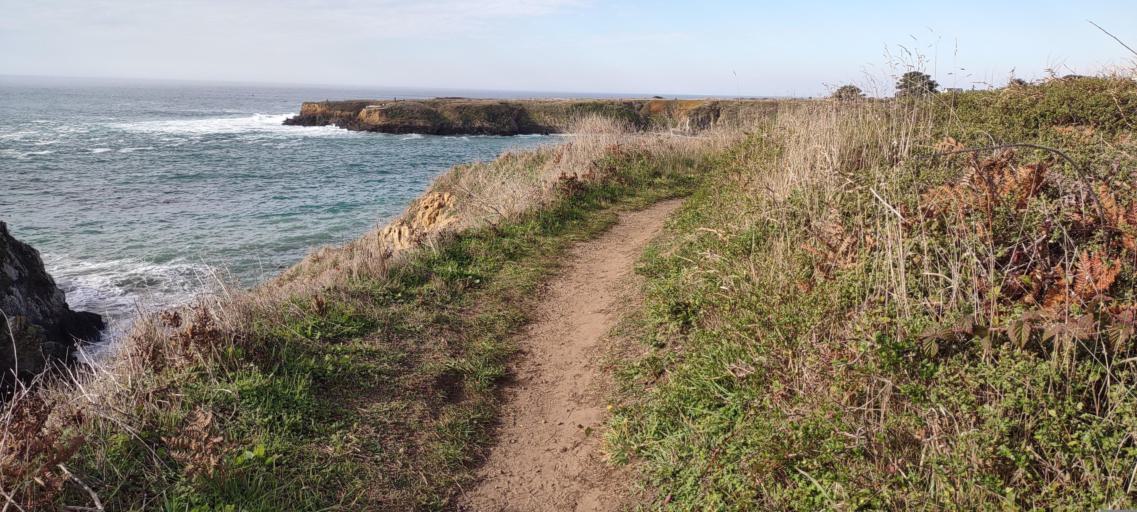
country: US
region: California
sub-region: Mendocino County
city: Fort Bragg
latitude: 39.3034
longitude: -123.7998
